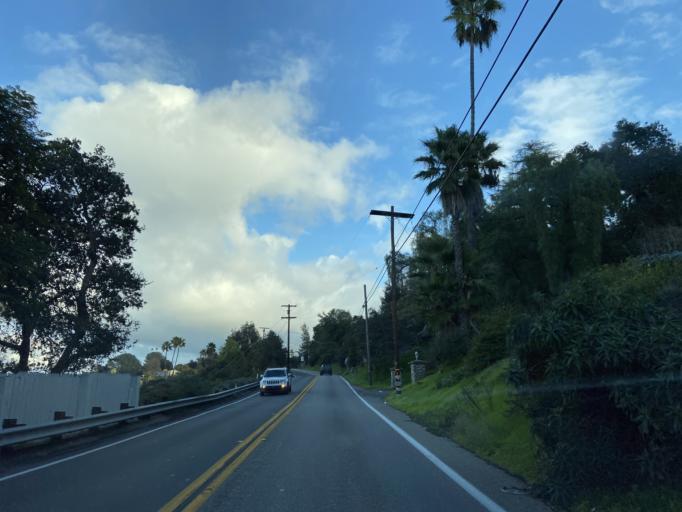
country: US
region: California
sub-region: San Diego County
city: Casa de Oro-Mount Helix
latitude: 32.7766
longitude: -116.9906
